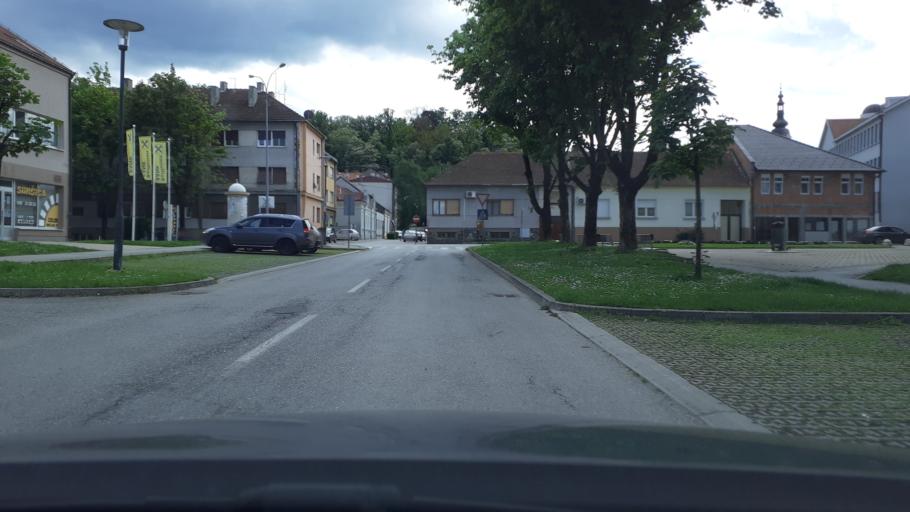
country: HR
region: Pozesko-Slavonska
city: Pozega
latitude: 45.3351
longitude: 17.6808
